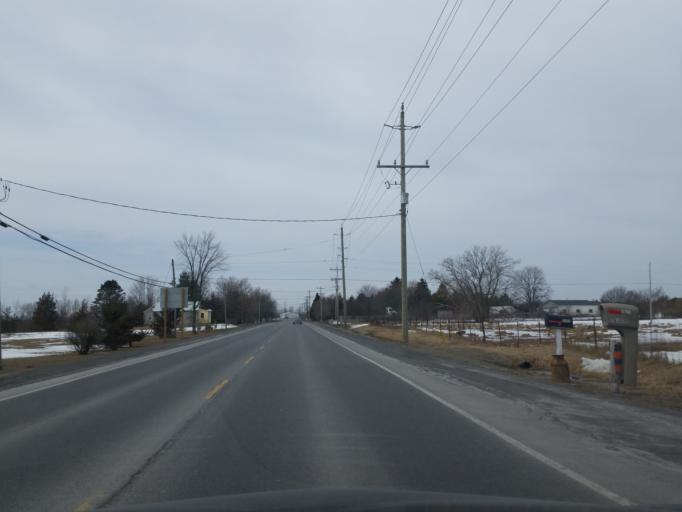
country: CA
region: Ontario
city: Skatepark
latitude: 44.2744
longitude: -76.7395
